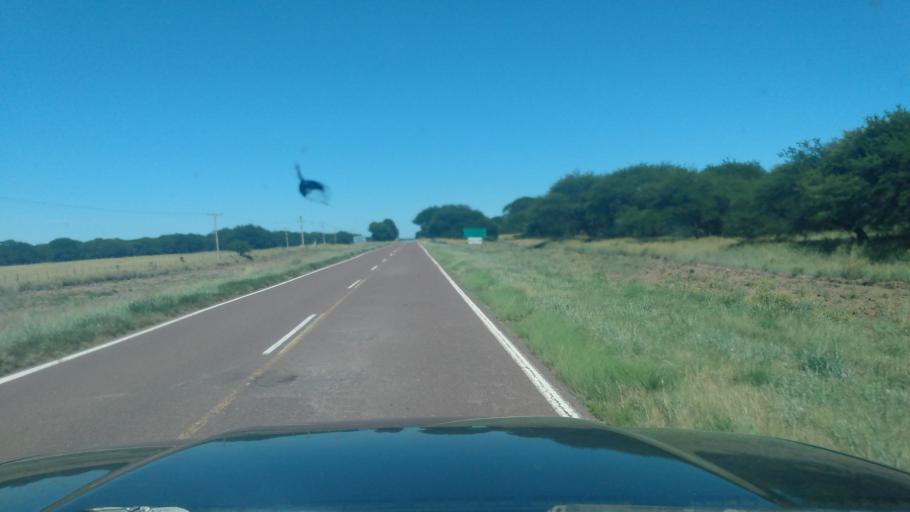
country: AR
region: La Pampa
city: General Acha
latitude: -37.4172
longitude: -64.8512
